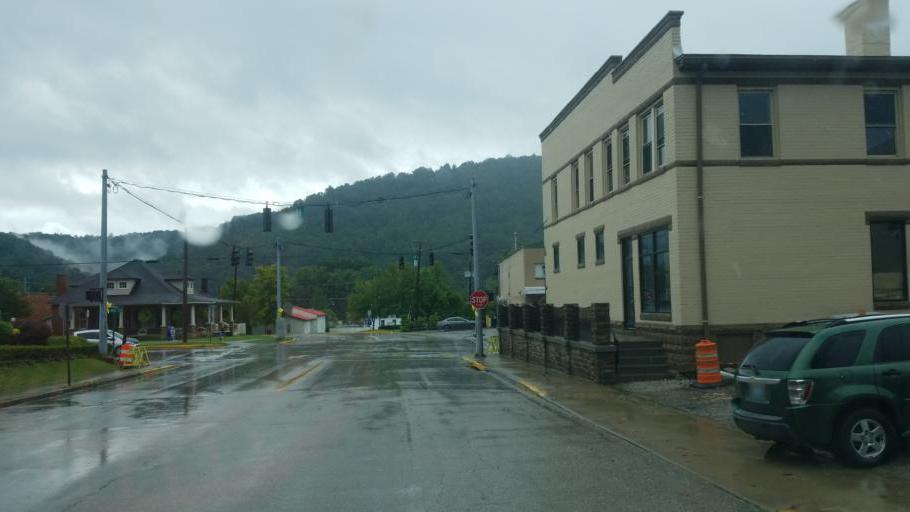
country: US
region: Kentucky
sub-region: Rowan County
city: Morehead
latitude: 38.1841
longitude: -83.4341
